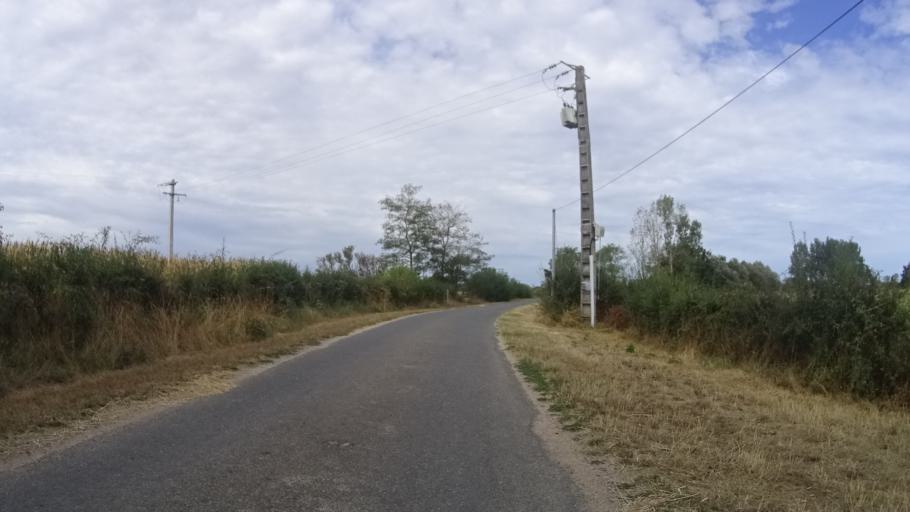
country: FR
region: Auvergne
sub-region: Departement de l'Allier
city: Beaulon
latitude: 46.6546
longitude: 3.6634
